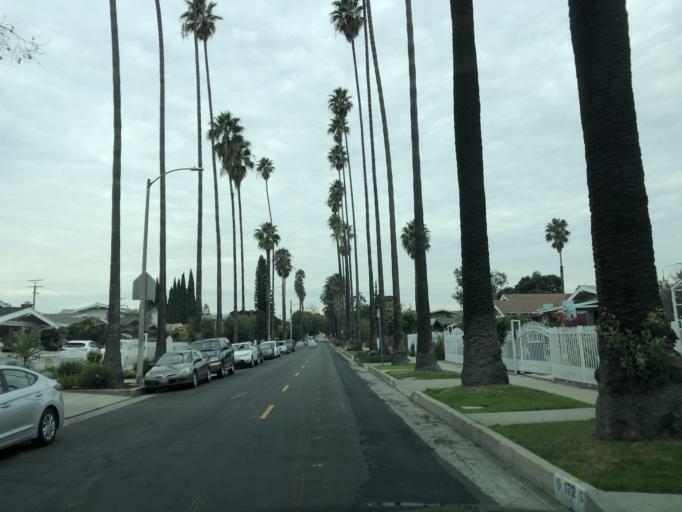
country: US
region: California
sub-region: Los Angeles County
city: Hollywood
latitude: 34.0715
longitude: -118.3055
